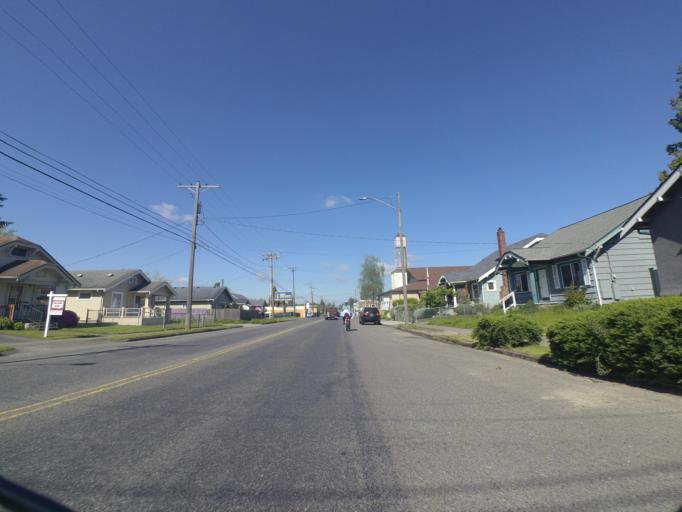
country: US
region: Washington
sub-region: Pierce County
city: Tacoma
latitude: 47.2065
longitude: -122.4486
